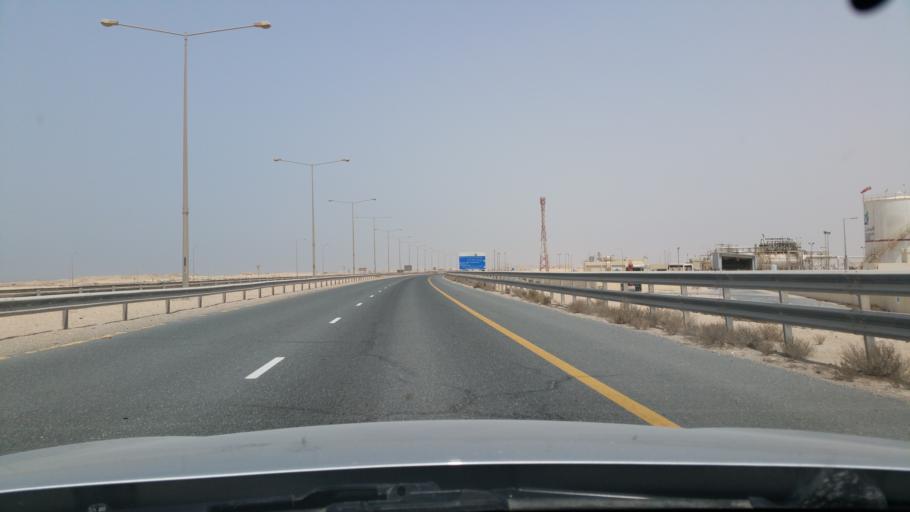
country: QA
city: Umm Bab
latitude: 25.2306
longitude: 50.8028
